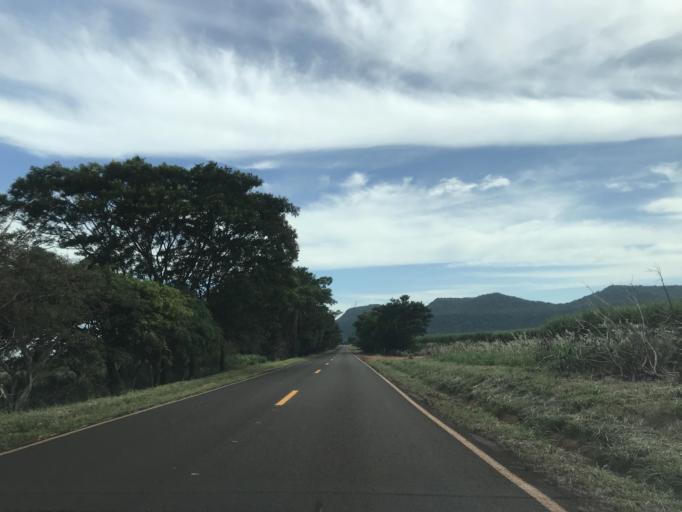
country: BR
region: Parana
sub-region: Paranavai
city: Nova Aurora
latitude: -22.8101
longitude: -52.6542
